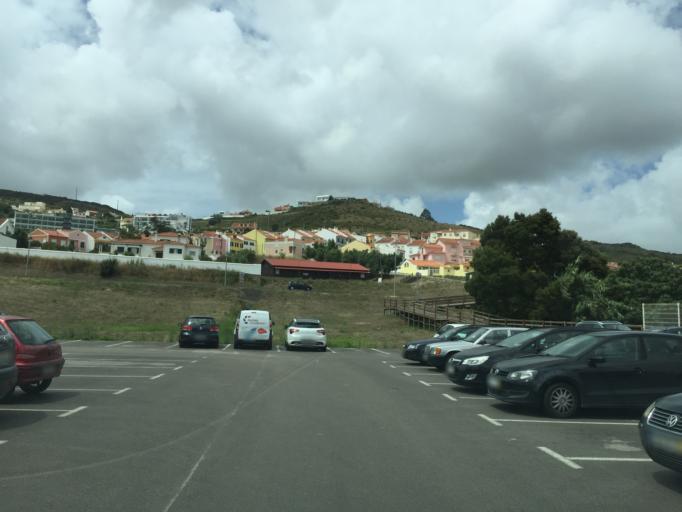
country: PT
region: Lisbon
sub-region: Torres Vedras
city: Torres Vedras
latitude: 39.0887
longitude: -9.2631
